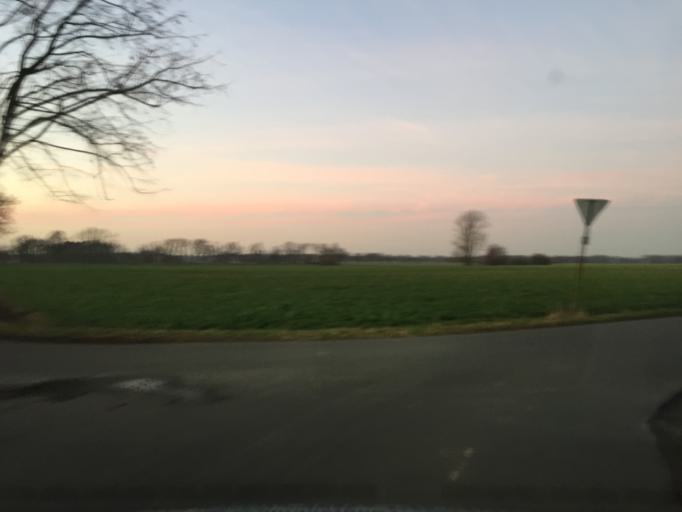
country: DE
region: Lower Saxony
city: Barenburg
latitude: 52.6435
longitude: 8.8303
